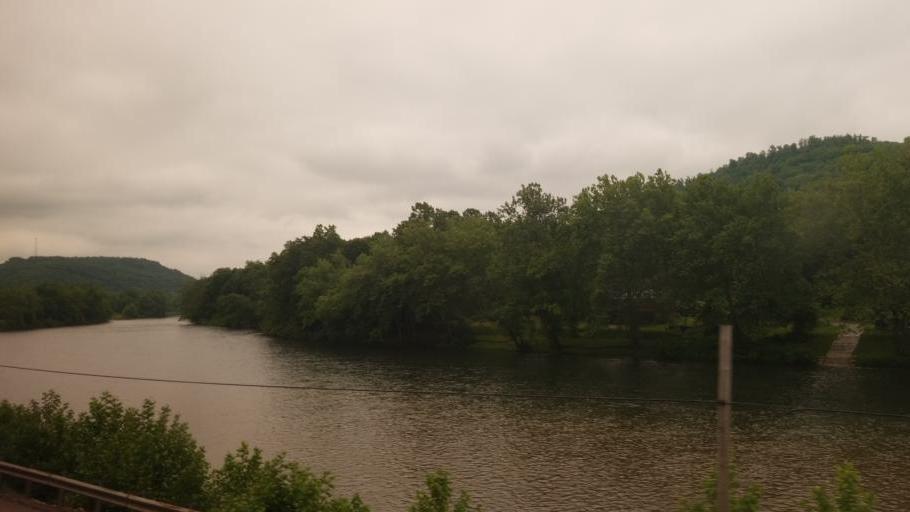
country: US
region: Pennsylvania
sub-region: Fayette County
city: South Connellsville
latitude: 39.8226
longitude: -79.3660
